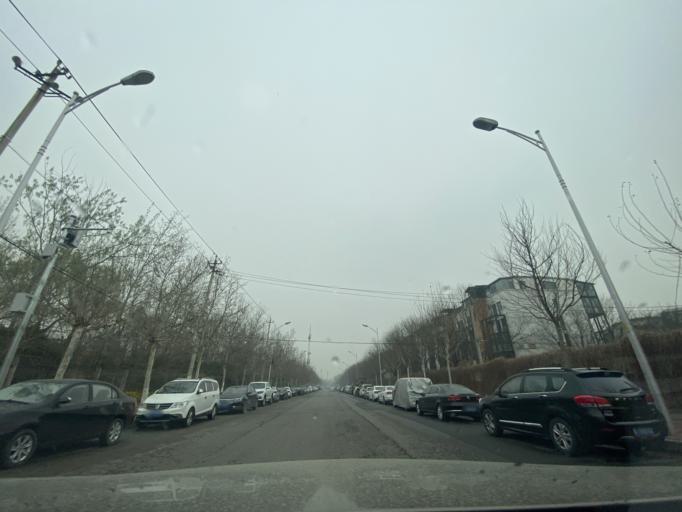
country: CN
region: Beijing
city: Sijiqing
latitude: 39.9583
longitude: 116.2308
